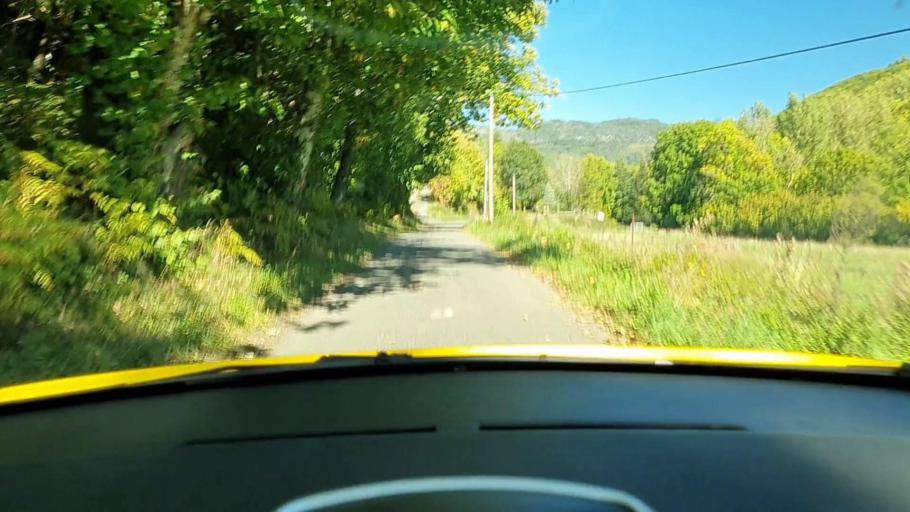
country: FR
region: Languedoc-Roussillon
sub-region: Departement du Gard
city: Le Vigan
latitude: 43.9801
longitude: 3.4437
